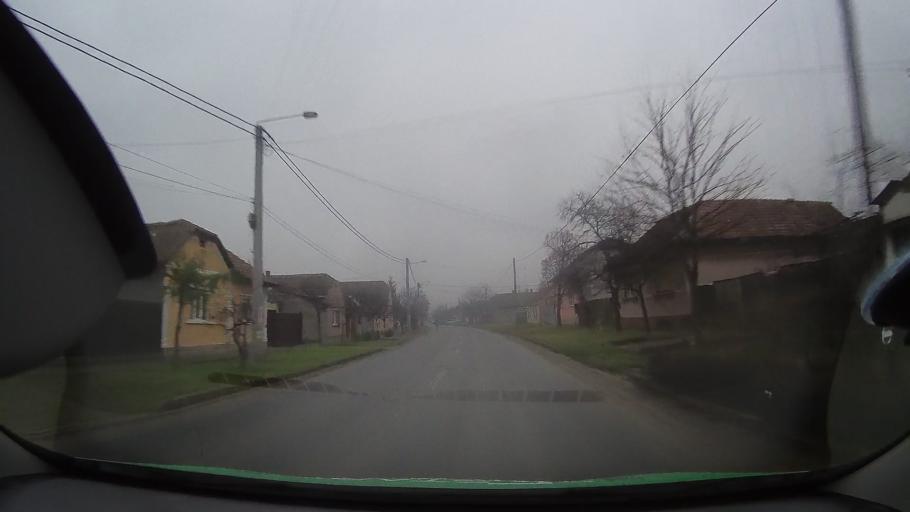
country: RO
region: Bihor
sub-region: Municipiul Salonta
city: Salonta
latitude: 46.7964
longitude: 21.6583
